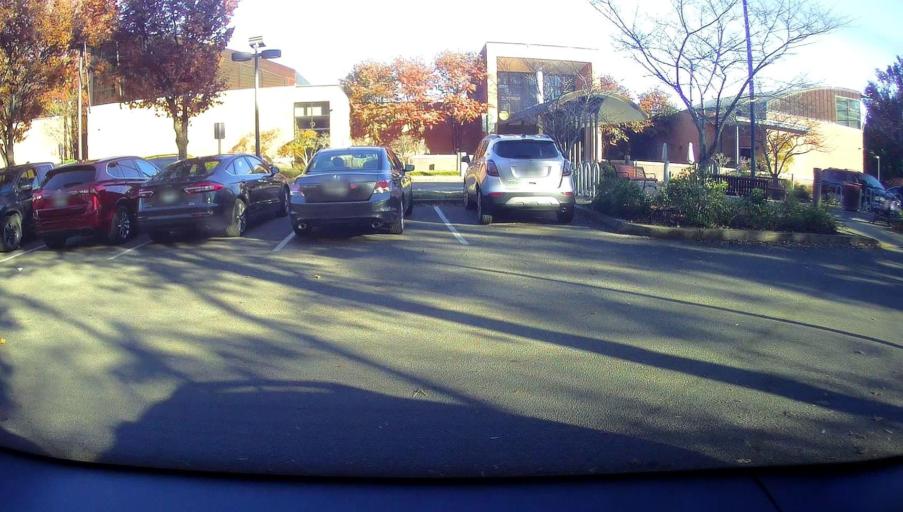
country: US
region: Tennessee
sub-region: Shelby County
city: Germantown
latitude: 35.0967
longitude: -89.8037
